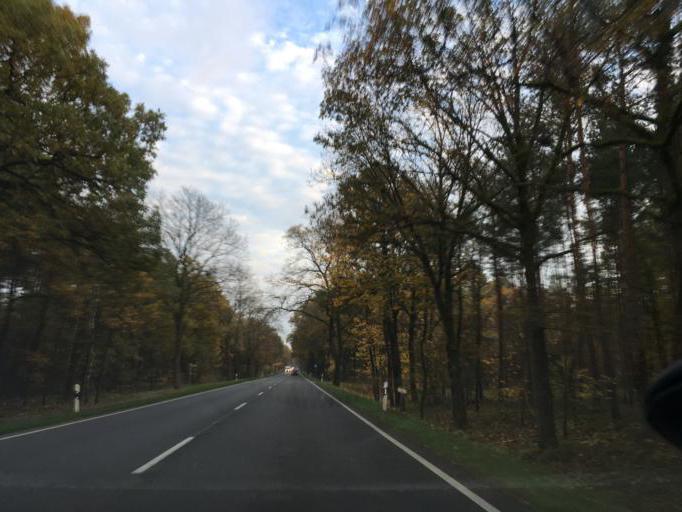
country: DE
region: Lower Saxony
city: Hambuhren
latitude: 52.6751
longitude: 10.0210
